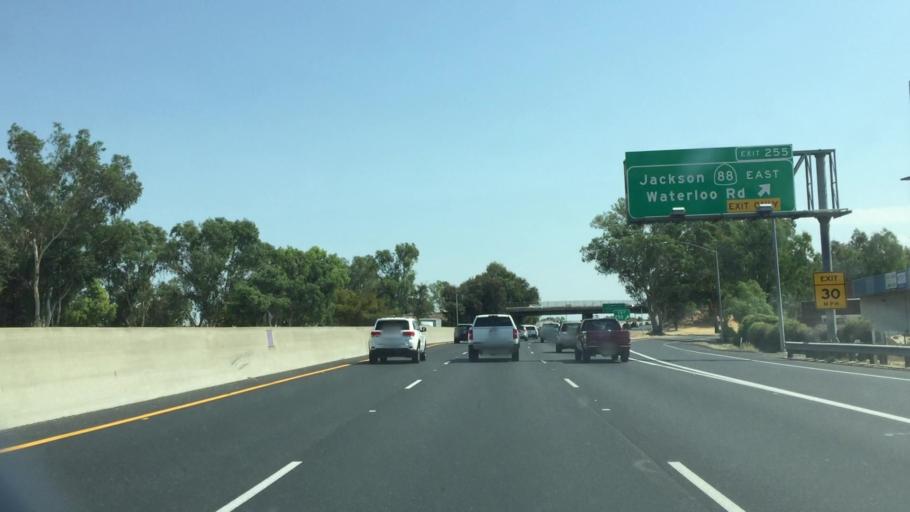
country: US
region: California
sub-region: San Joaquin County
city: August
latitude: 37.9871
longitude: -121.2508
